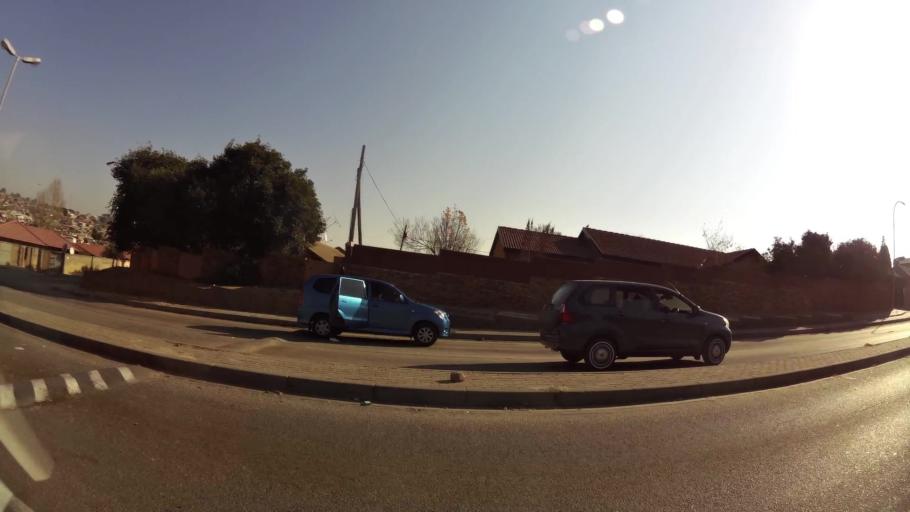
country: ZA
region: Gauteng
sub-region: City of Johannesburg Metropolitan Municipality
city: Modderfontein
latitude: -26.1053
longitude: 28.1094
